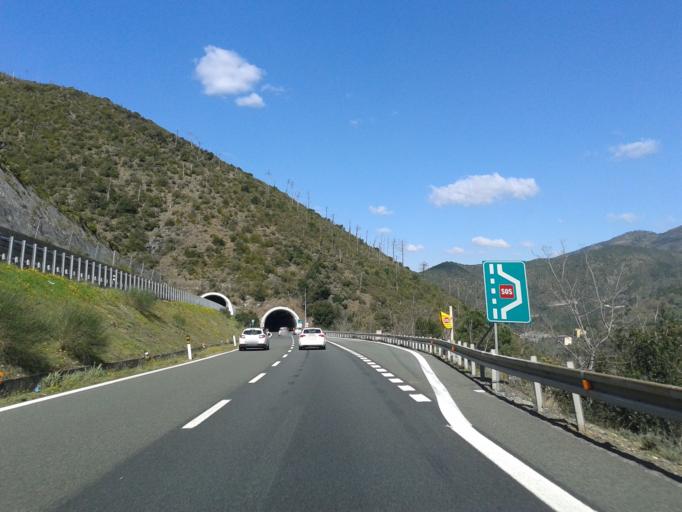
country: IT
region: Liguria
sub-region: Provincia di Genova
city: Moneglia
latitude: 44.2671
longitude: 9.4796
